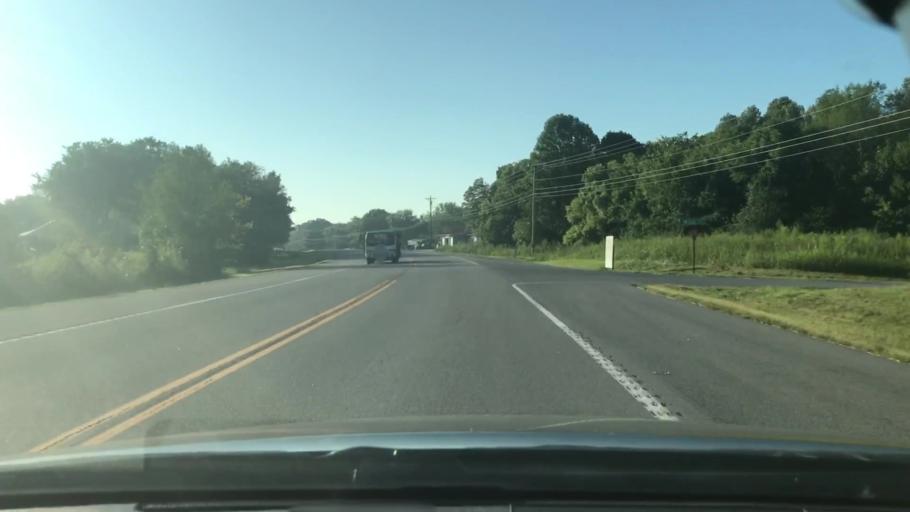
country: US
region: Tennessee
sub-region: Sumner County
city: Millersville
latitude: 36.4138
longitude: -86.7106
